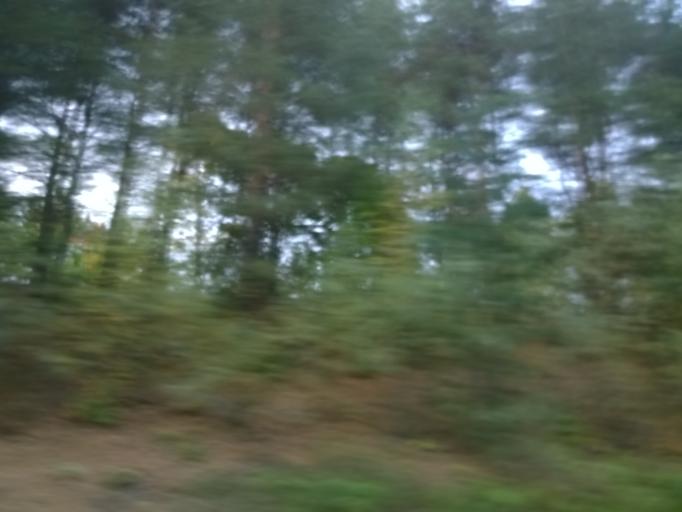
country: FI
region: Pirkanmaa
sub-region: Tampere
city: Tampere
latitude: 61.5002
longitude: 23.8088
